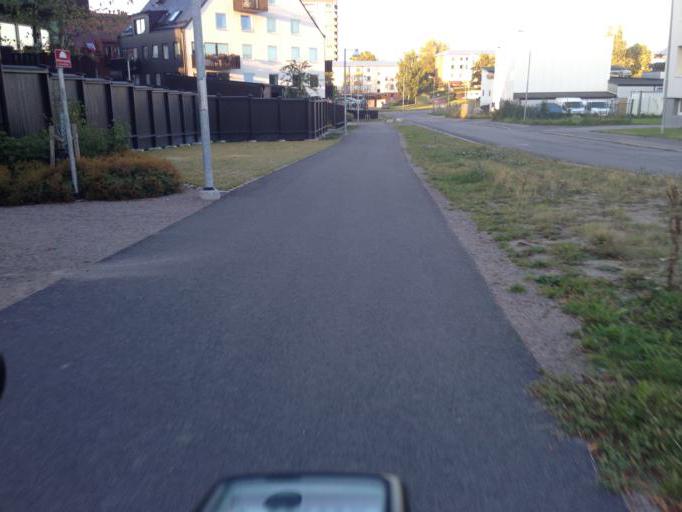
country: SE
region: OEstergoetland
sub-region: Norrkopings Kommun
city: Norrkoping
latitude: 58.5814
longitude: 16.1620
